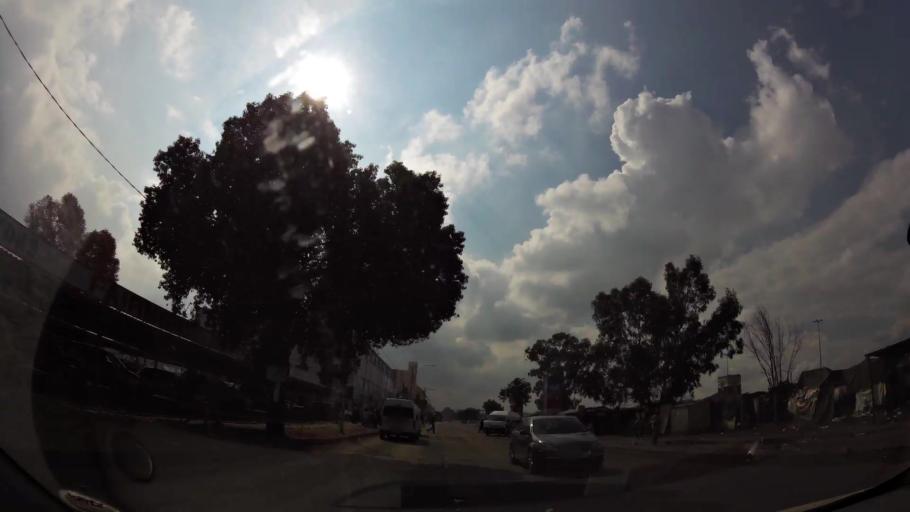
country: ZA
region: Gauteng
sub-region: Sedibeng District Municipality
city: Vereeniging
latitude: -26.6728
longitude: 27.9342
